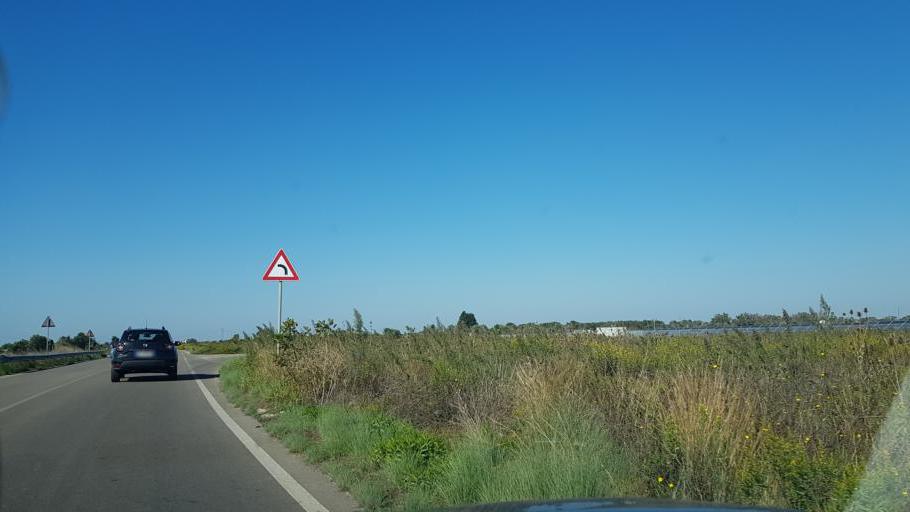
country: IT
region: Apulia
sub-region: Provincia di Lecce
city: Carmiano
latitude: 40.3136
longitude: 18.0397
